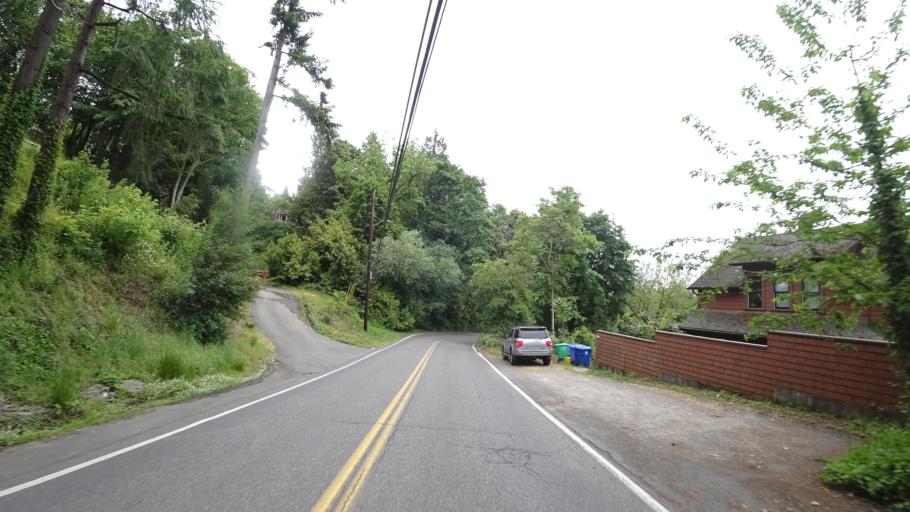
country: US
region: Oregon
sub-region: Multnomah County
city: Portland
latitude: 45.5060
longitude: -122.6956
